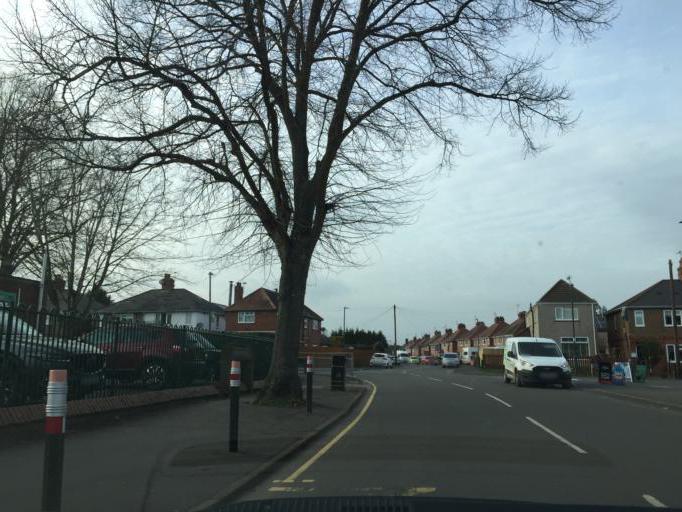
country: GB
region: England
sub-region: Warwickshire
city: Kenilworth
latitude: 52.3361
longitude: -1.5797
